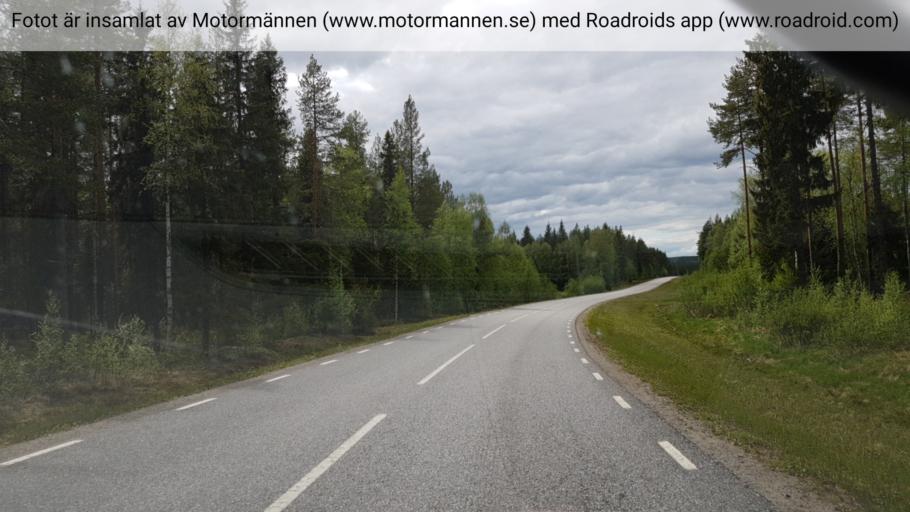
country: SE
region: Vaesterbotten
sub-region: Skelleftea Kommun
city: Langsele
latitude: 64.6123
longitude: 19.9610
